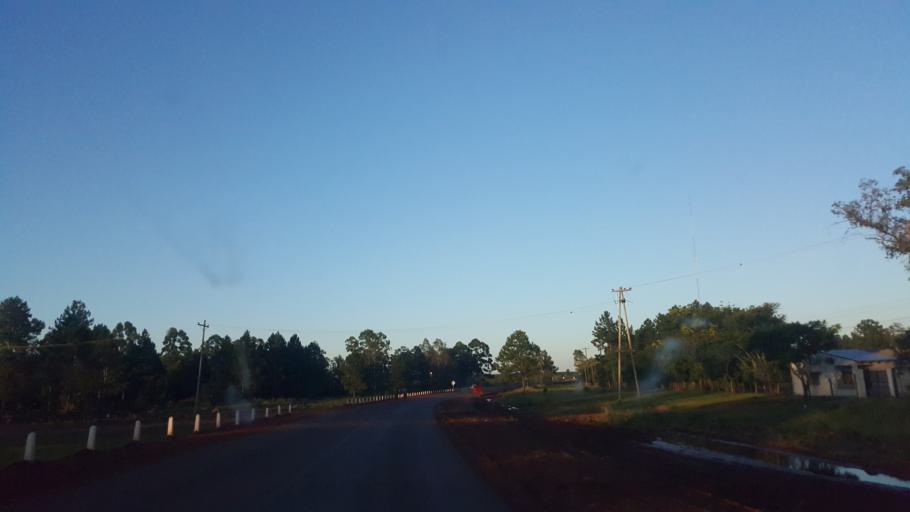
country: AR
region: Corrientes
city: Santo Tome
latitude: -28.5084
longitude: -56.0595
